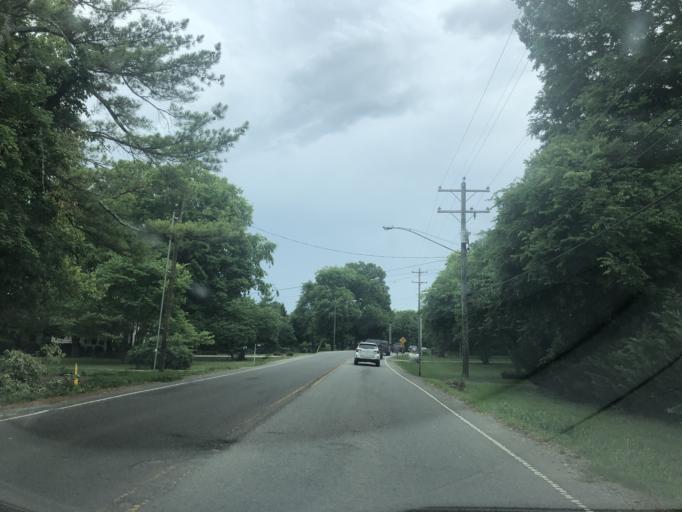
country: US
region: Tennessee
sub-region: Davidson County
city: Oak Hill
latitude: 36.0882
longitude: -86.7879
